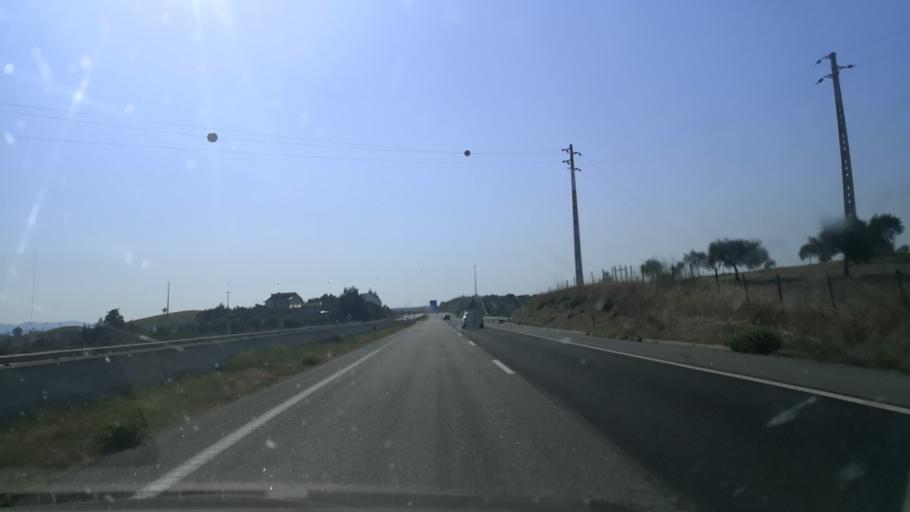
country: PT
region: Braganca
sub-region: Mirandela
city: Mirandela
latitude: 41.5170
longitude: -7.1608
